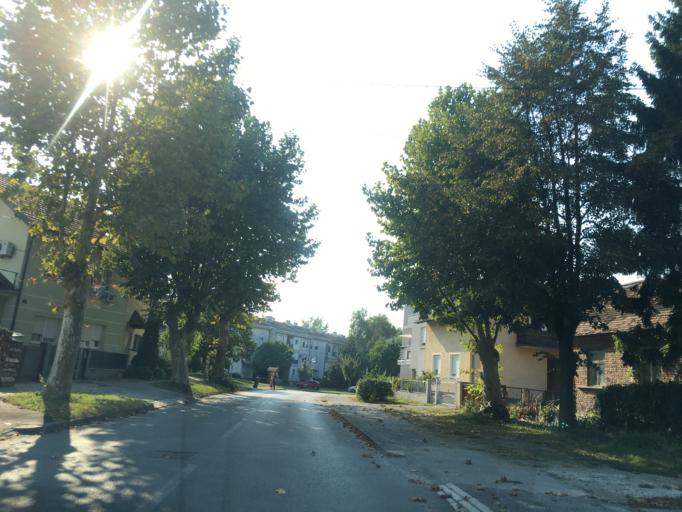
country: HR
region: Grad Zagreb
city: Jankomir
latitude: 45.7858
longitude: 15.9224
